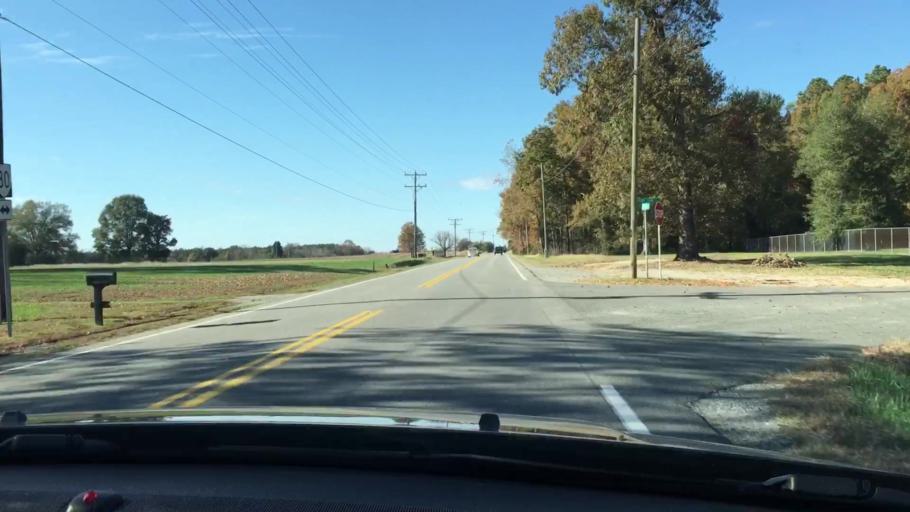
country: US
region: Virginia
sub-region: King William County
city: Central Garage
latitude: 37.7215
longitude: -77.0828
